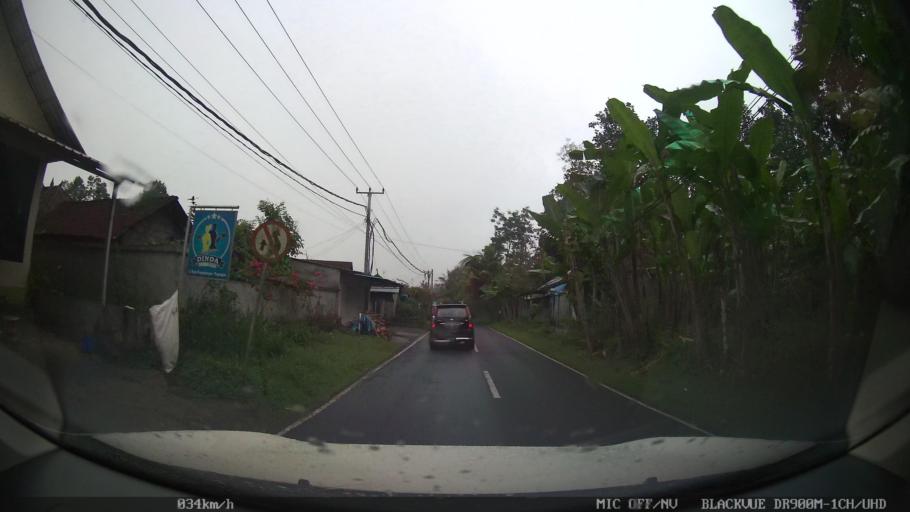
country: ID
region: Bali
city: Banjar Taro Kelod
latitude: -8.3618
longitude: 115.2716
